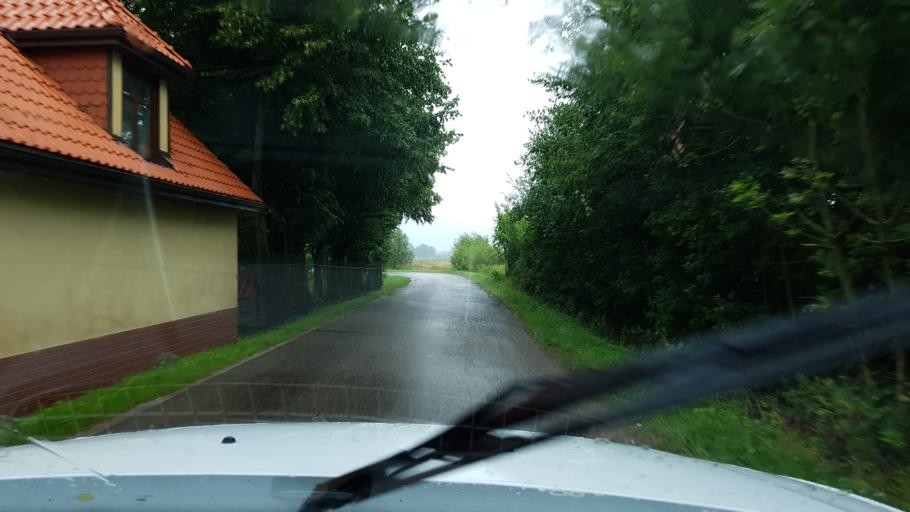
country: PL
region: West Pomeranian Voivodeship
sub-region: Powiat kolobrzeski
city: Ustronie Morskie
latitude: 54.2143
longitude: 15.8604
